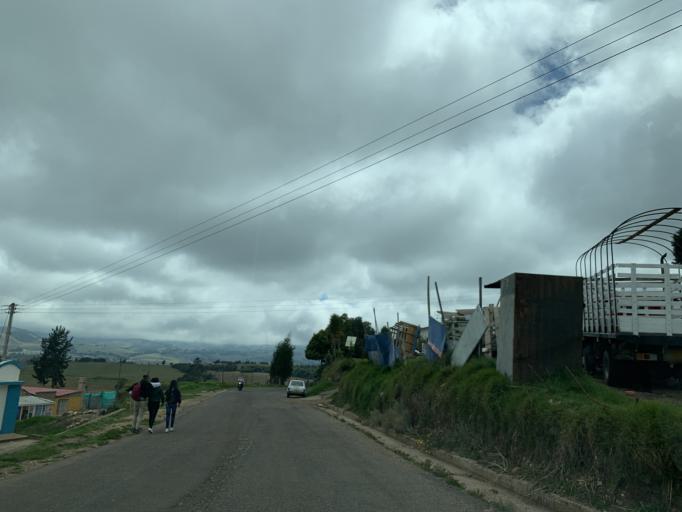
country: CO
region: Boyaca
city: Tunja
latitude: 5.5800
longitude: -73.3570
